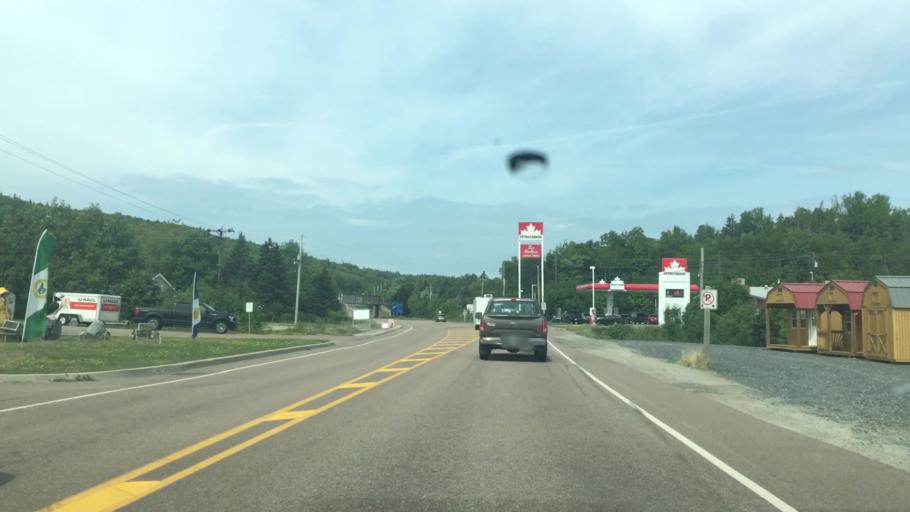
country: CA
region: Nova Scotia
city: Port Hawkesbury
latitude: 45.6522
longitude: -61.4438
